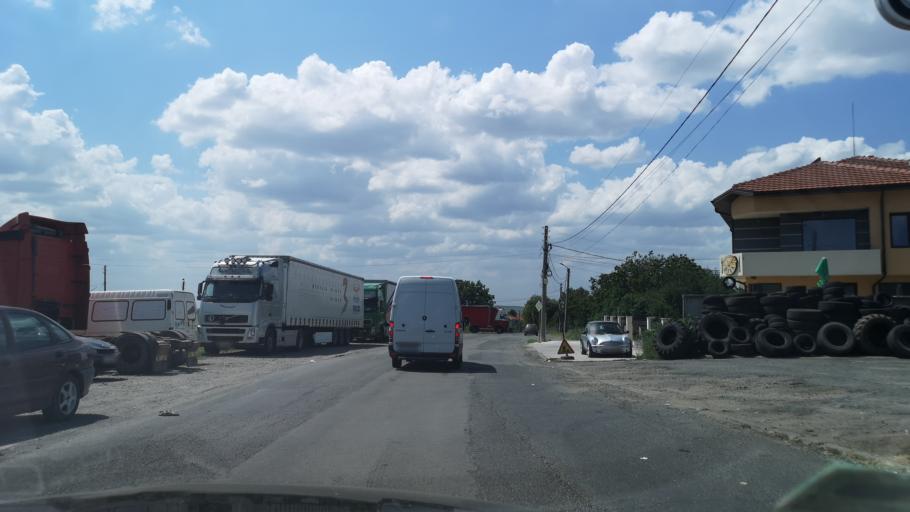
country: BG
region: Burgas
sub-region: Obshtina Kameno
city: Kameno
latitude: 42.6168
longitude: 27.3093
